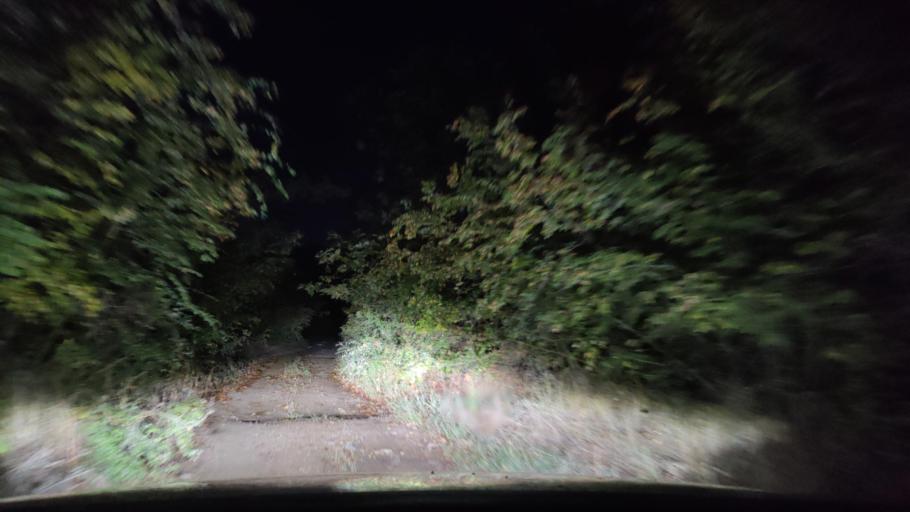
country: GR
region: Central Macedonia
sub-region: Nomos Serron
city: Chrysochorafa
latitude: 41.2327
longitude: 23.1048
